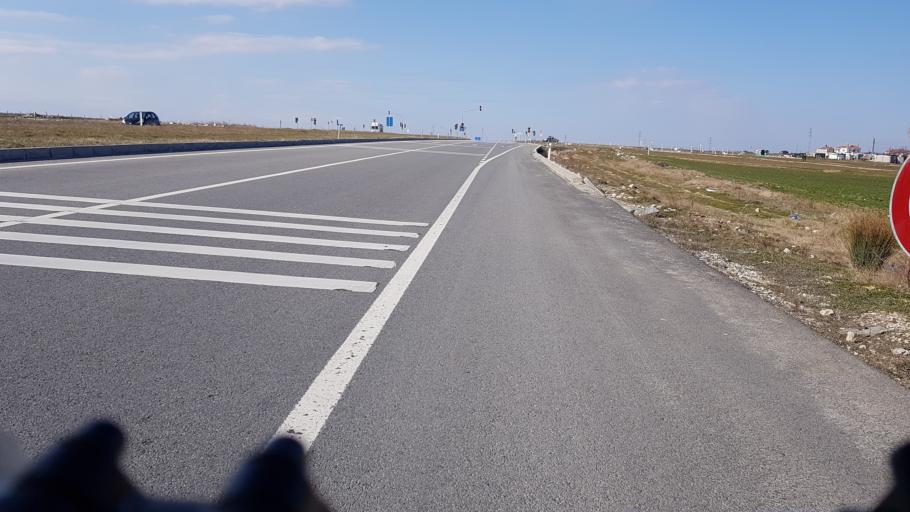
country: TR
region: Tekirdag
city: Saray
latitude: 41.4297
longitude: 27.9104
